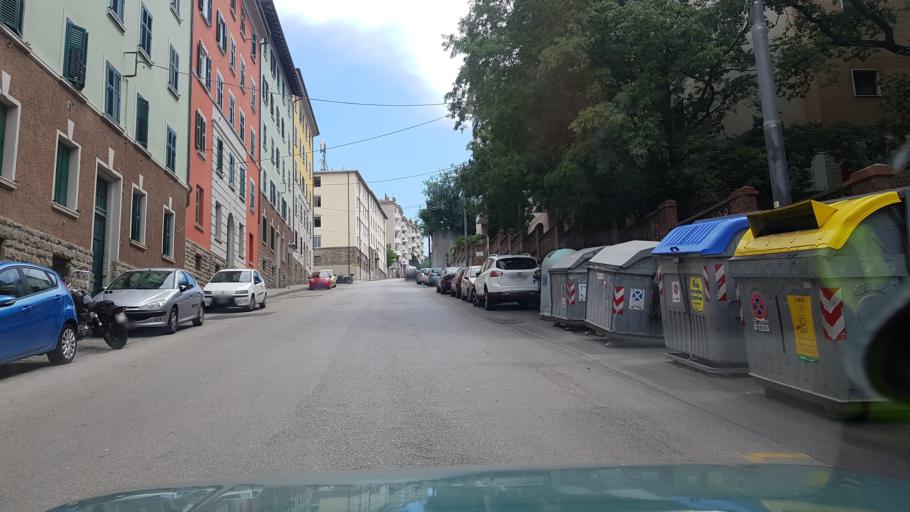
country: IT
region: Friuli Venezia Giulia
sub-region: Provincia di Trieste
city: Trieste
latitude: 45.6534
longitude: 13.8053
